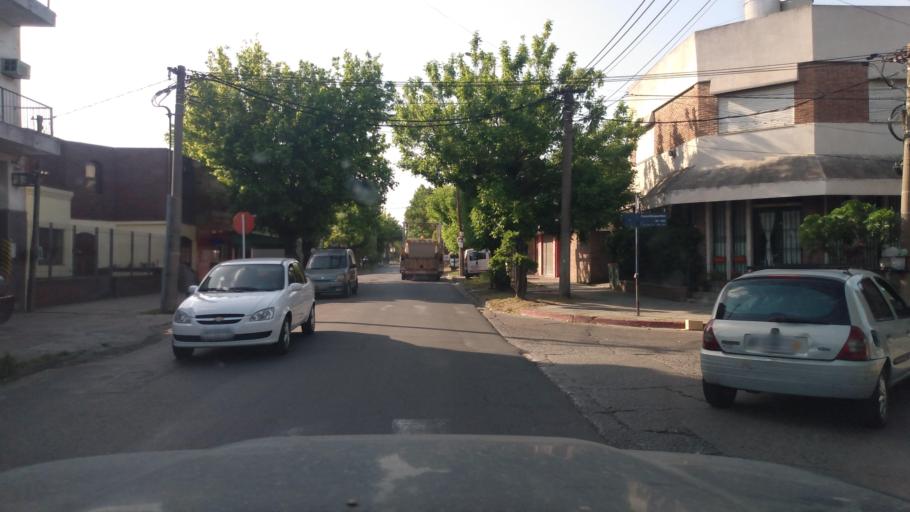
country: AR
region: Buenos Aires
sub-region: Partido de Moron
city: Moron
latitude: -34.6423
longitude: -58.6147
